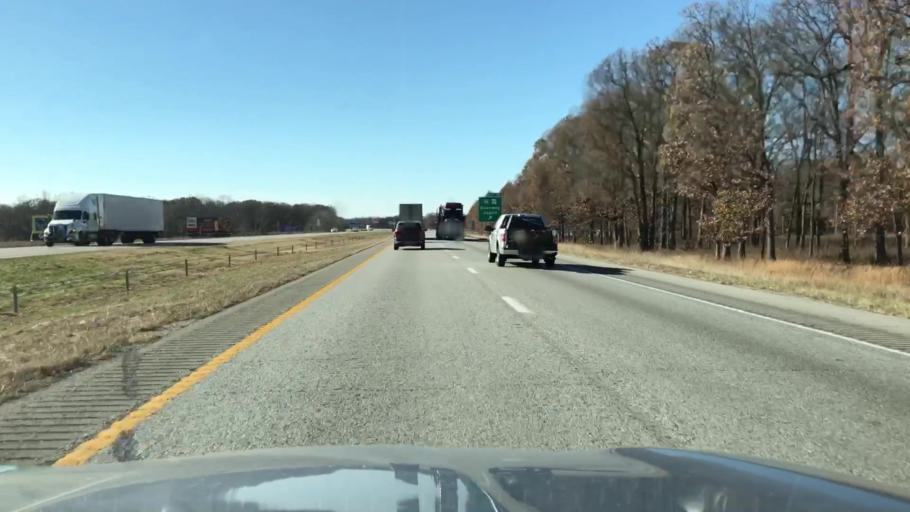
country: US
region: Missouri
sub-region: Jasper County
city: Duenweg
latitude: 37.0823
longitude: -94.3560
